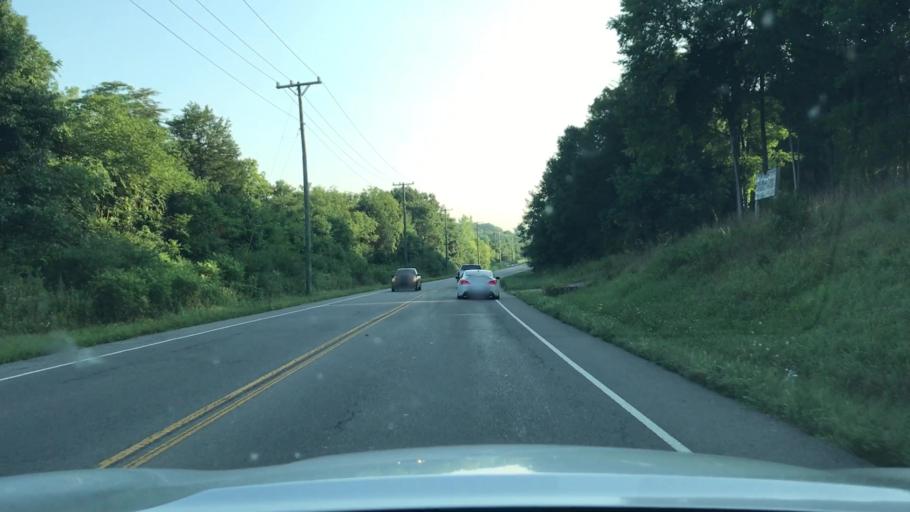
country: US
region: Tennessee
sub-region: Rutherford County
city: La Vergne
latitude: 35.9972
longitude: -86.6240
